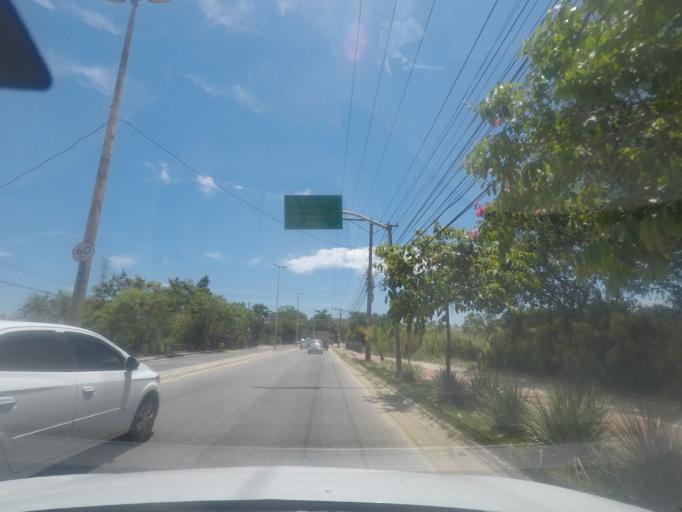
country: BR
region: Rio de Janeiro
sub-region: Itaguai
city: Itaguai
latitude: -22.9010
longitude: -43.6807
